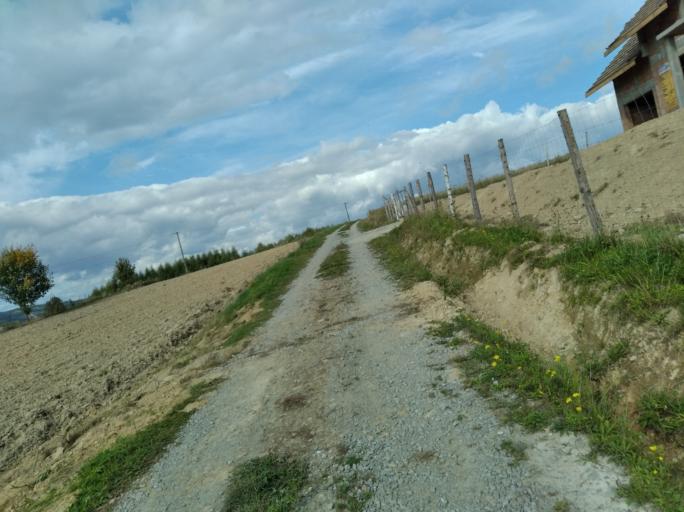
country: PL
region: Subcarpathian Voivodeship
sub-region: Powiat strzyzowski
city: Jawornik
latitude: 49.8335
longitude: 21.9015
